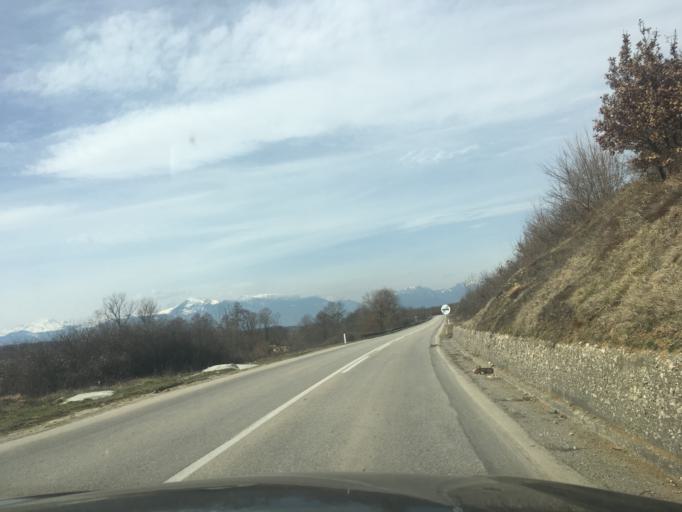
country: XK
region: Pec
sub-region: Komuna e Klines
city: Klina
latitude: 42.5937
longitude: 20.5445
